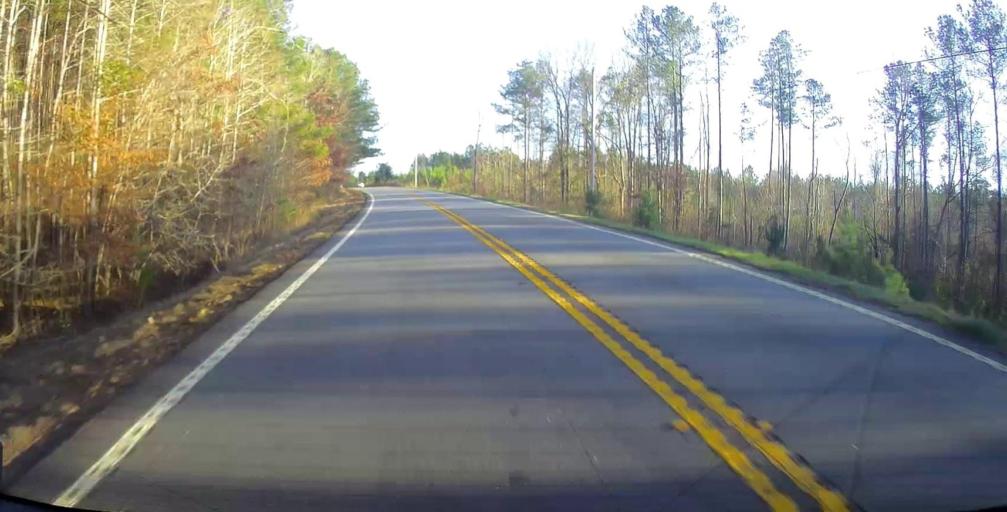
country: US
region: Alabama
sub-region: Chambers County
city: Valley
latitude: 32.7922
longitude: -85.1014
